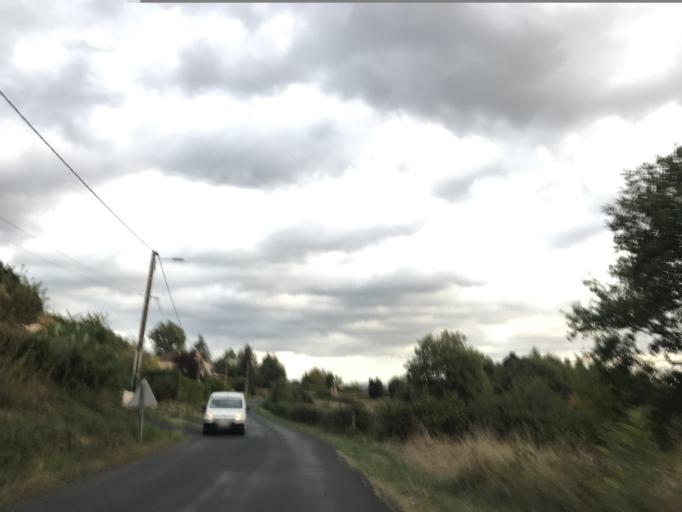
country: FR
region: Auvergne
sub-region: Departement du Puy-de-Dome
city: Escoutoux
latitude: 45.8290
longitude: 3.5516
